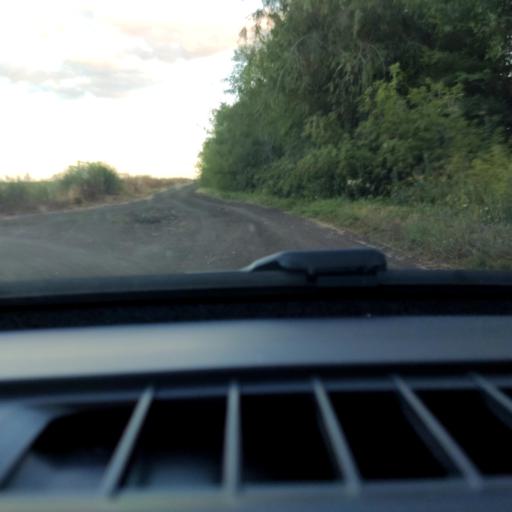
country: RU
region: Voronezj
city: Verkhnyaya Khava
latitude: 51.6063
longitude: 39.8369
